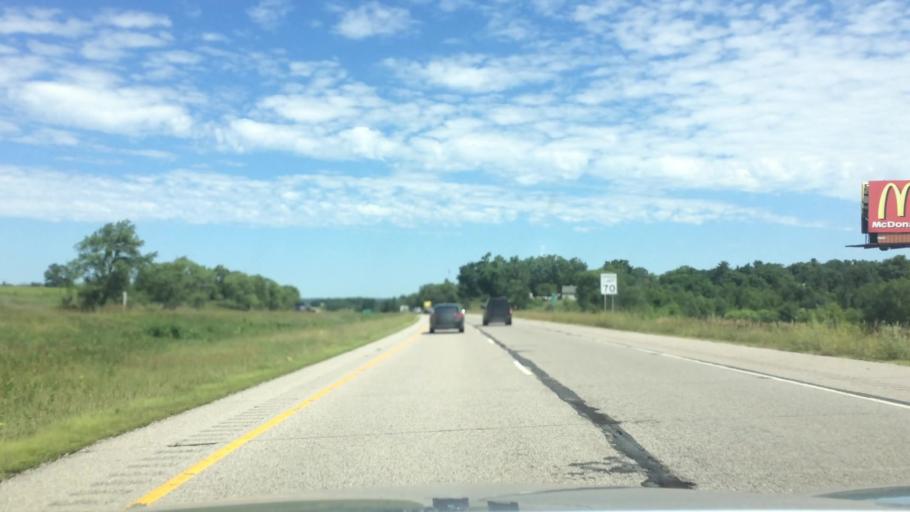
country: US
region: Wisconsin
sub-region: Columbia County
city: Portage
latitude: 43.7105
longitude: -89.4730
